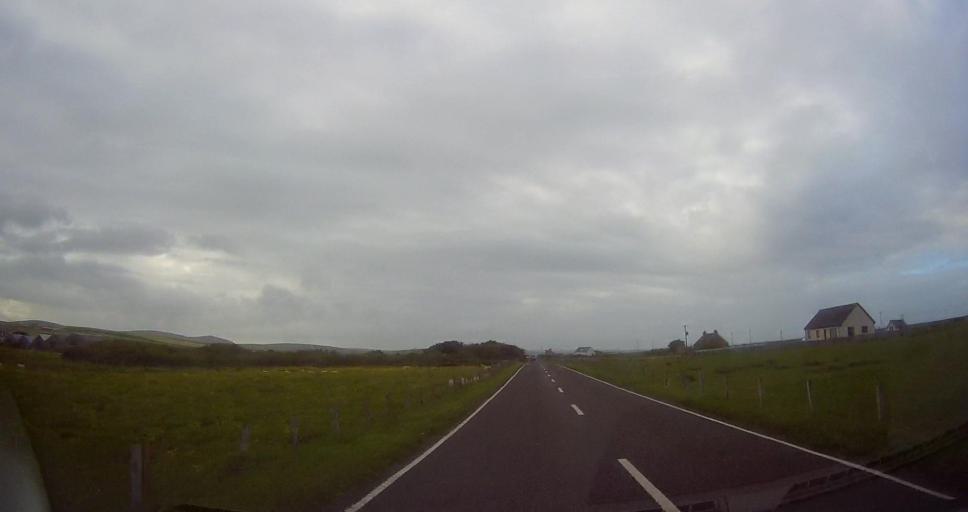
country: GB
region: Scotland
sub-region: Orkney Islands
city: Stromness
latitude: 58.9747
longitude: -3.2398
